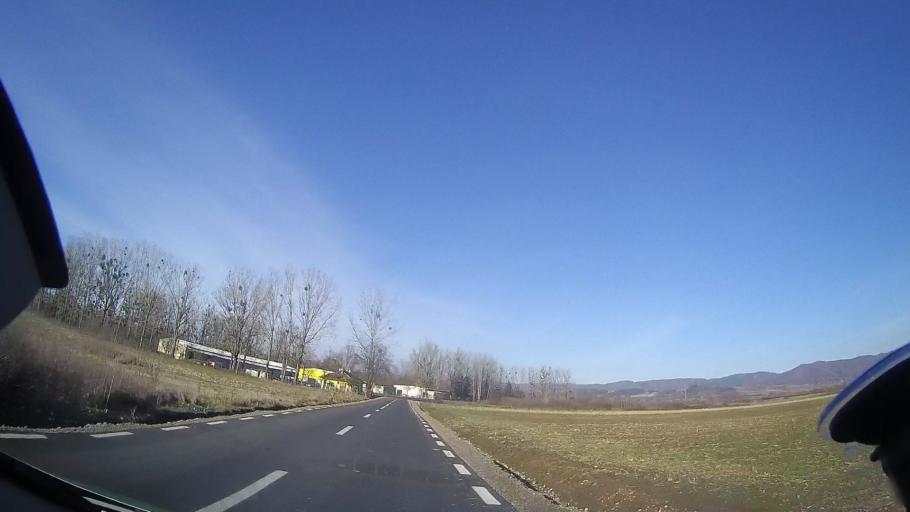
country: RO
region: Bihor
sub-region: Comuna Vadu Crisului
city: Vadu Crisului
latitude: 47.0033
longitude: 22.5019
